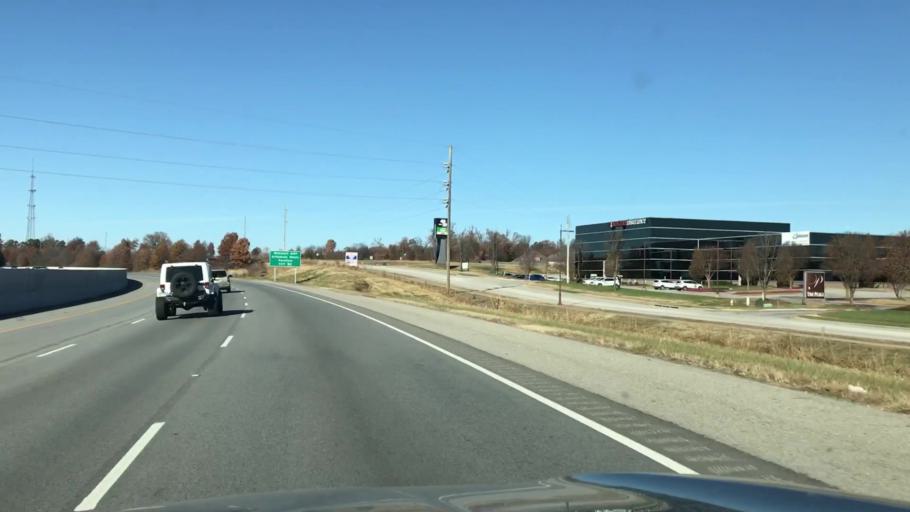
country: US
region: Arkansas
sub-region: Benton County
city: Lowell
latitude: 36.2942
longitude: -94.1647
